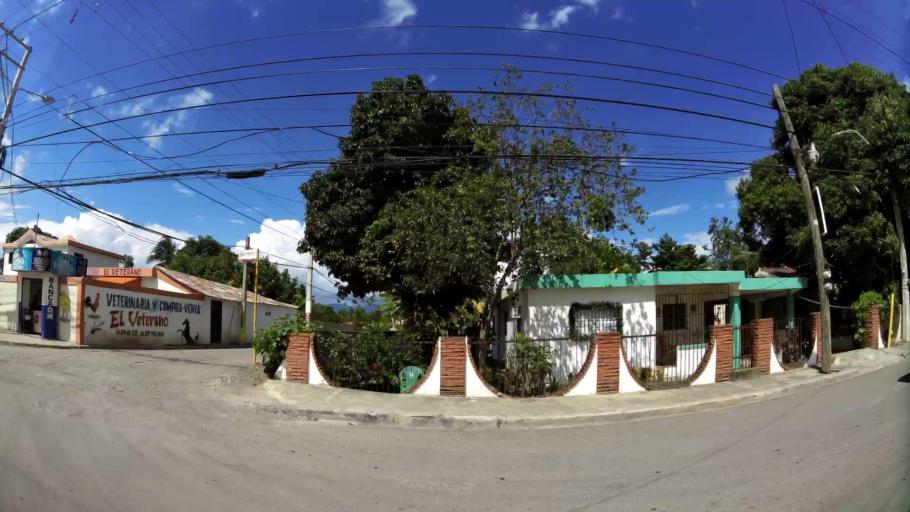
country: DO
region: Santiago
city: Licey al Medio
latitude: 19.3826
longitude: -70.6206
